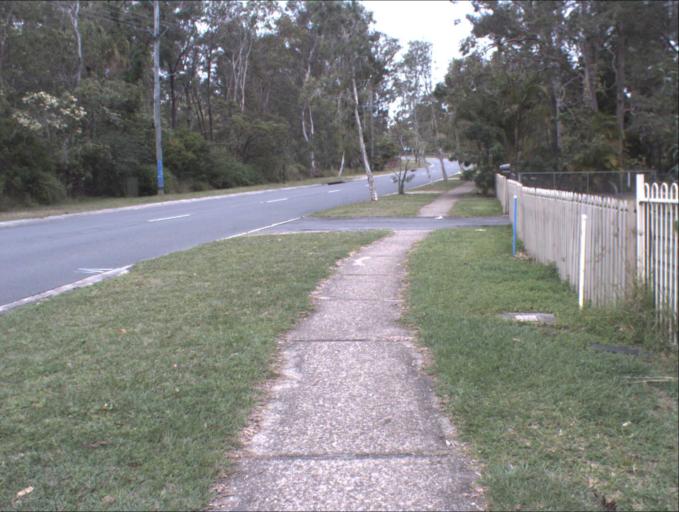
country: AU
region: Queensland
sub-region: Brisbane
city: Forest Lake
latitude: -27.6587
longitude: 153.0075
